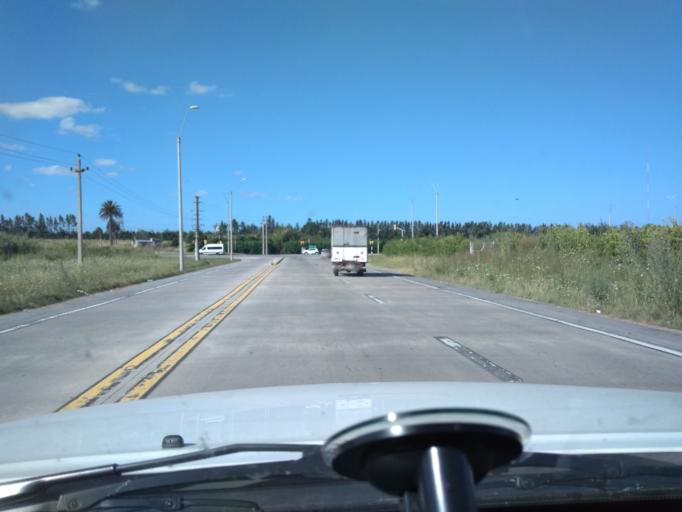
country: UY
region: Canelones
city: La Paz
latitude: -34.7922
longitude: -56.2115
